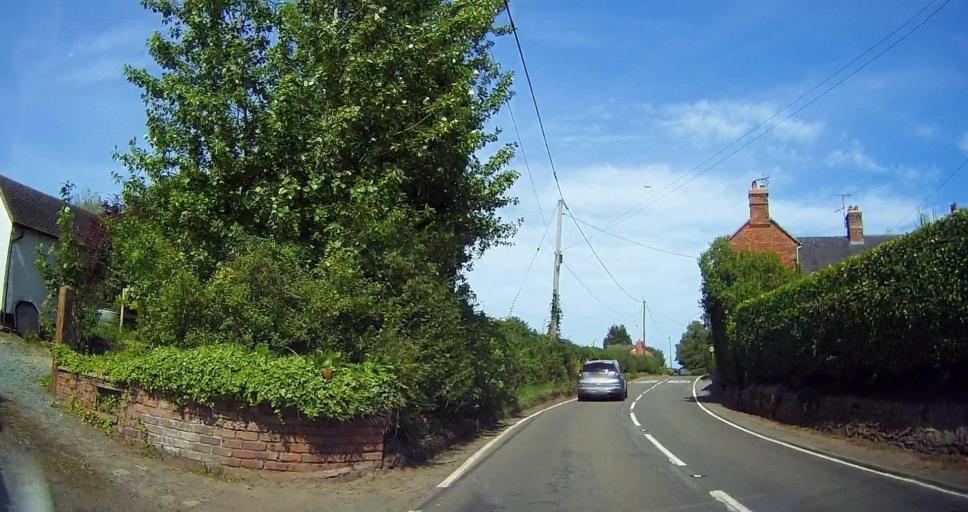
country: GB
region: England
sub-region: Shropshire
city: Market Drayton
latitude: 52.9763
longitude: -2.5153
